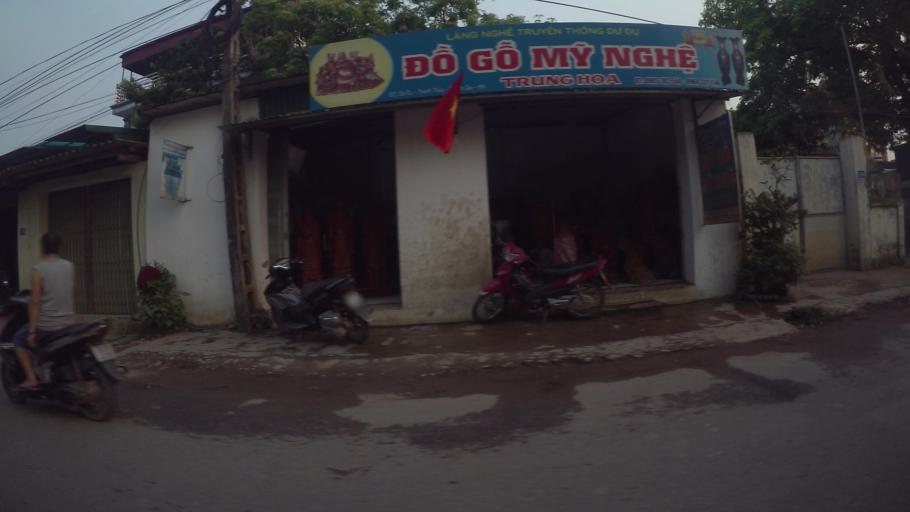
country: VN
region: Ha Noi
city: Thuong Tin
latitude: 20.8701
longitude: 105.8177
